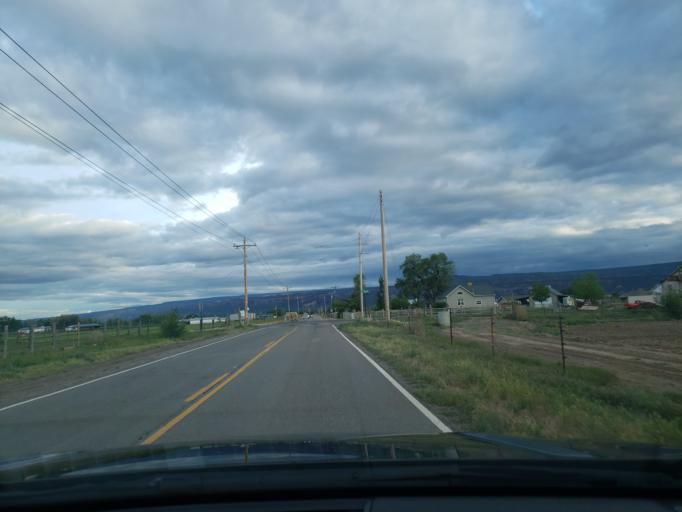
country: US
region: Colorado
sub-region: Mesa County
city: Fruita
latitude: 39.1938
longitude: -108.7012
